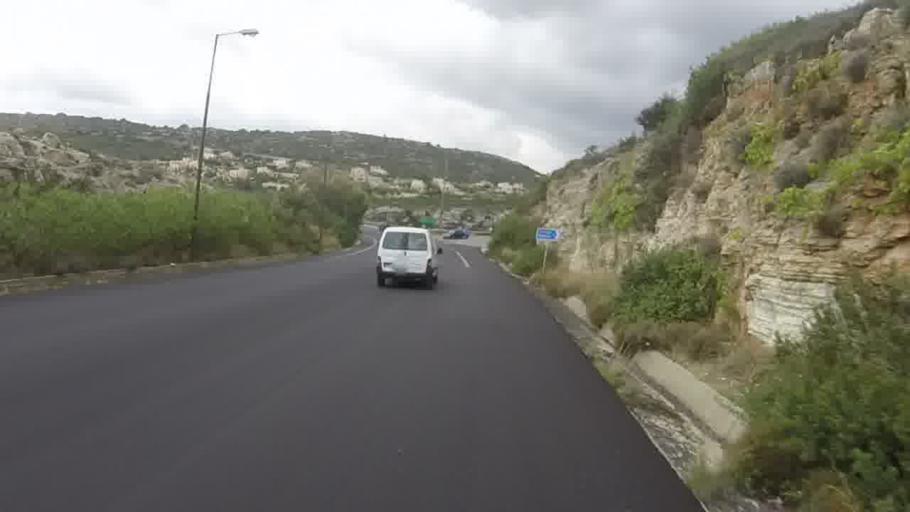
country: GR
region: Crete
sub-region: Nomos Rethymnis
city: Atsipopoulon
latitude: 35.3602
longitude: 24.4057
